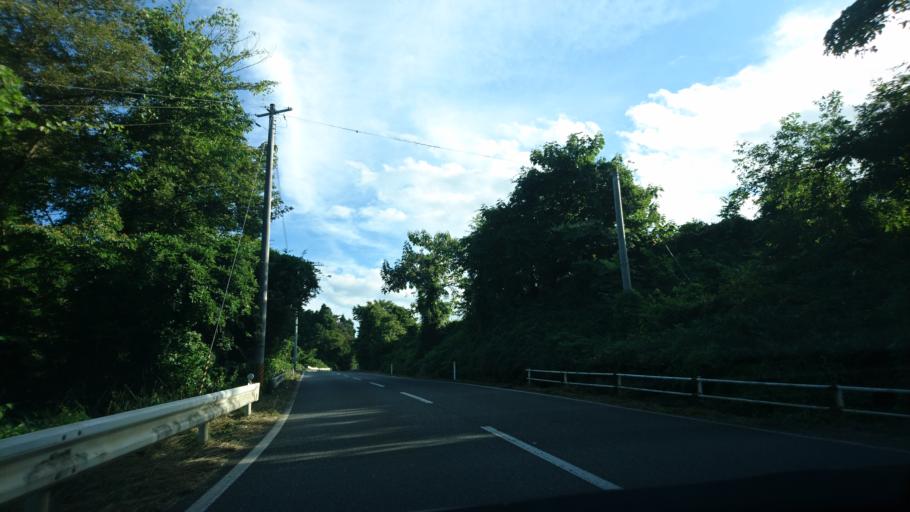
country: JP
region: Iwate
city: Ichinoseki
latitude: 38.8845
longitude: 141.2192
